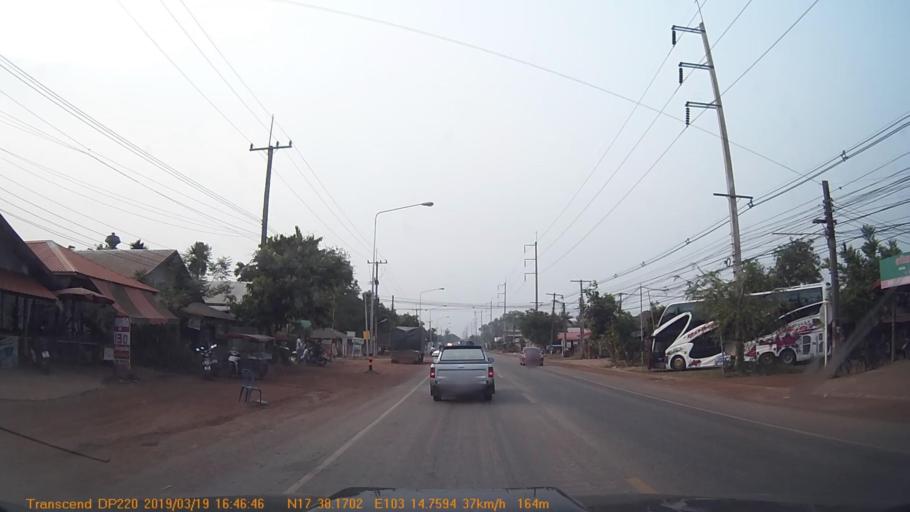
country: TH
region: Changwat Udon Thani
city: Ban Dung
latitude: 17.6364
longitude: 103.2459
